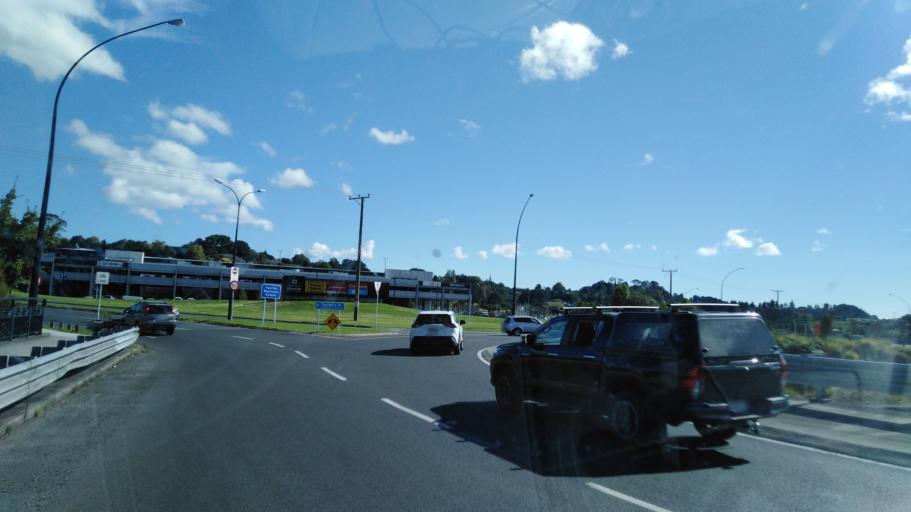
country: NZ
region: Bay of Plenty
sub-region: Tauranga City
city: Tauranga
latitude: -37.7389
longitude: 176.1077
